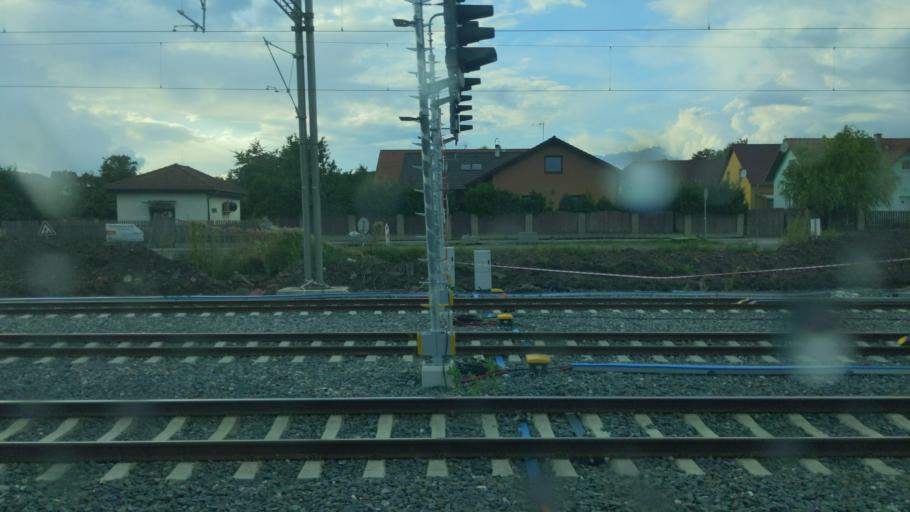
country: CZ
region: Central Bohemia
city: Poricany
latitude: 50.1100
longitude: 14.9188
